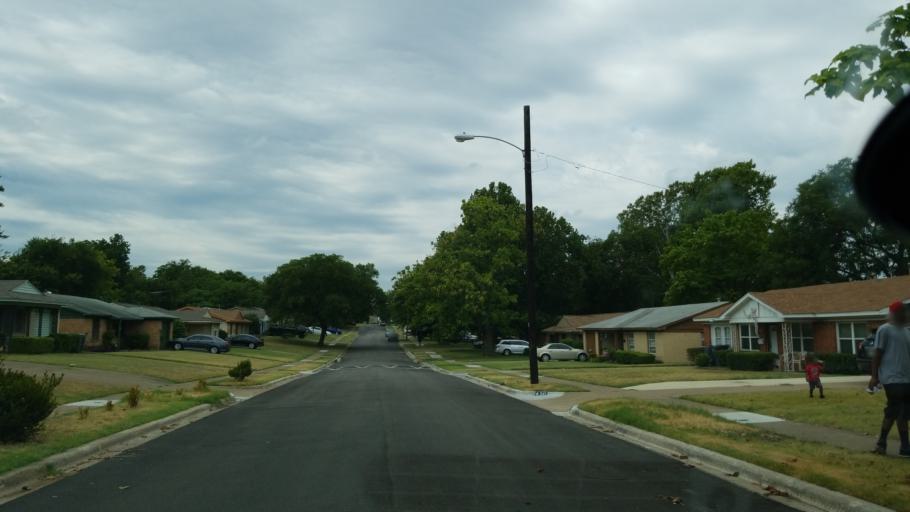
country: US
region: Texas
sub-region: Dallas County
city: Duncanville
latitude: 32.6607
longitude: -96.8363
